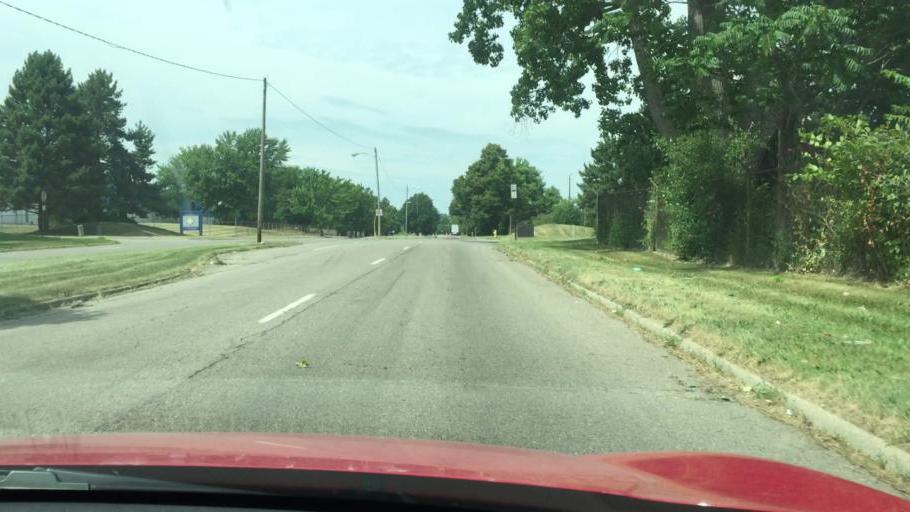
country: US
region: Michigan
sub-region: Genesee County
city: Flint
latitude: 43.0493
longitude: -83.6764
